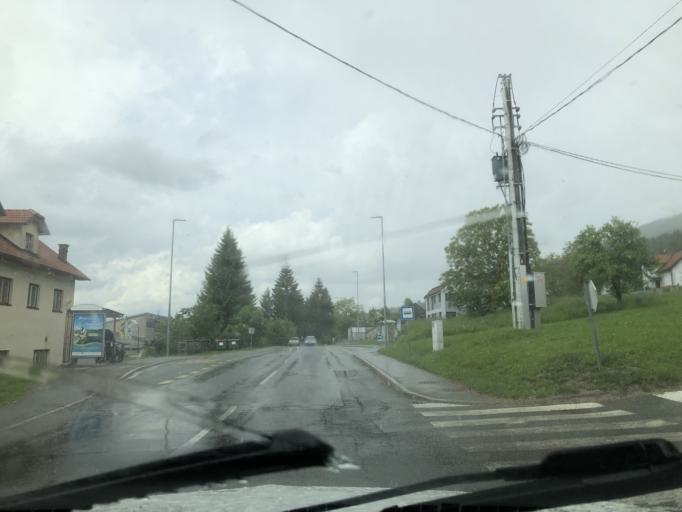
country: SI
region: Cerknica
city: Cerknica
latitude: 45.7761
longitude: 14.4022
